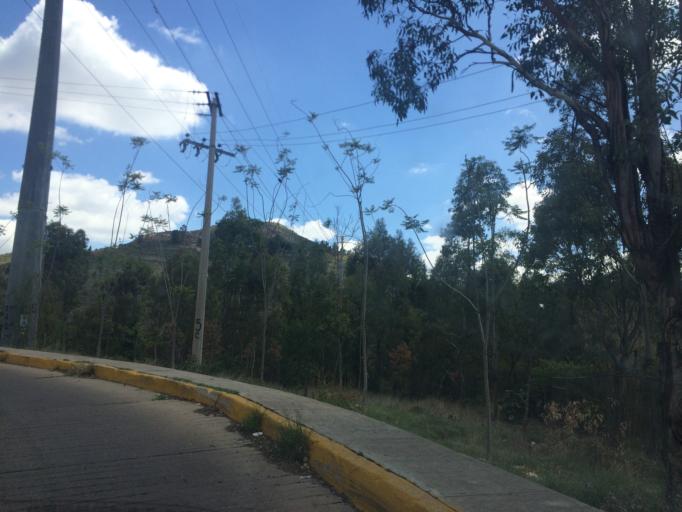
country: MX
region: Zacatecas
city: Zacatecas
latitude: 22.7585
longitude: -102.5804
